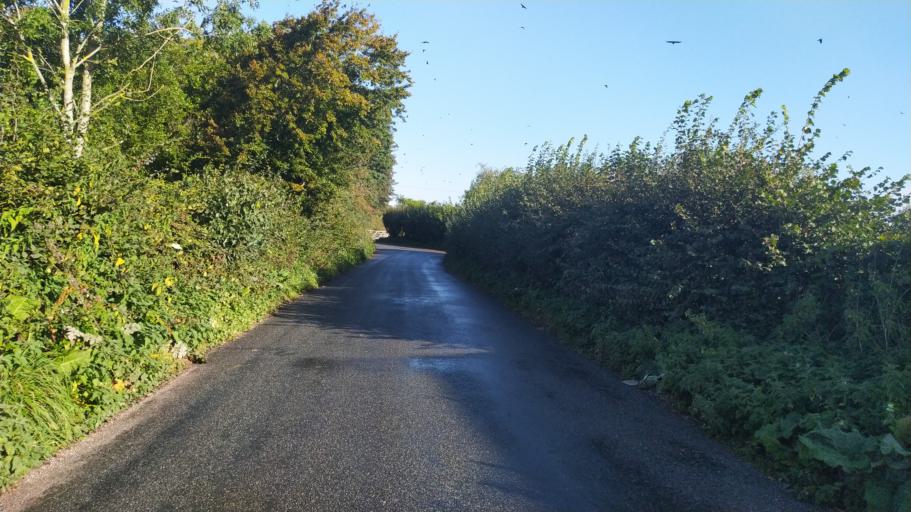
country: GB
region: England
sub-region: Dorset
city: Blandford Forum
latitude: 50.7750
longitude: -2.1669
